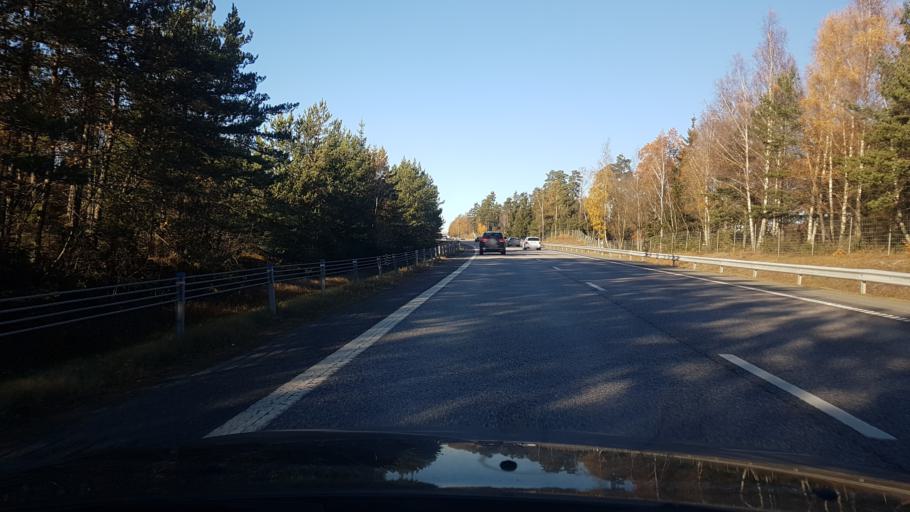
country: SE
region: Uppsala
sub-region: Knivsta Kommun
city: Knivsta
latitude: 59.7177
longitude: 17.8461
